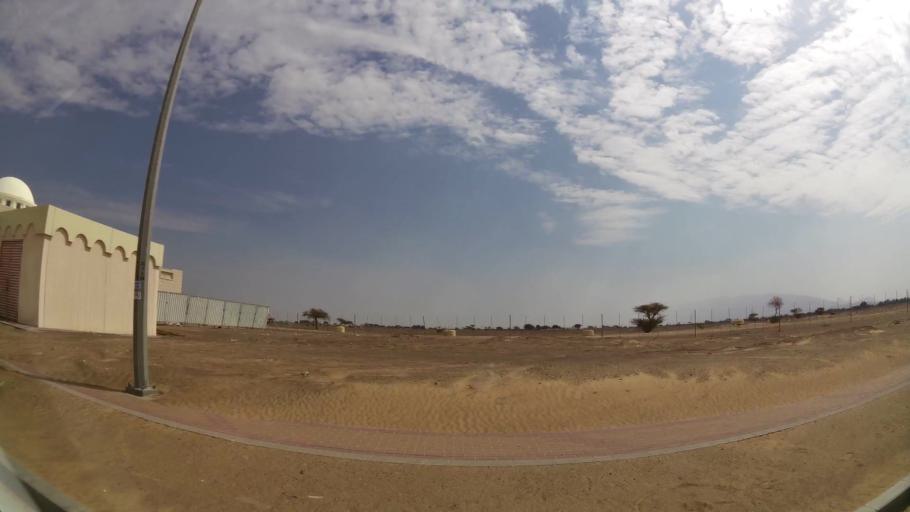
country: AE
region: Abu Dhabi
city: Al Ain
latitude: 24.1854
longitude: 55.8014
